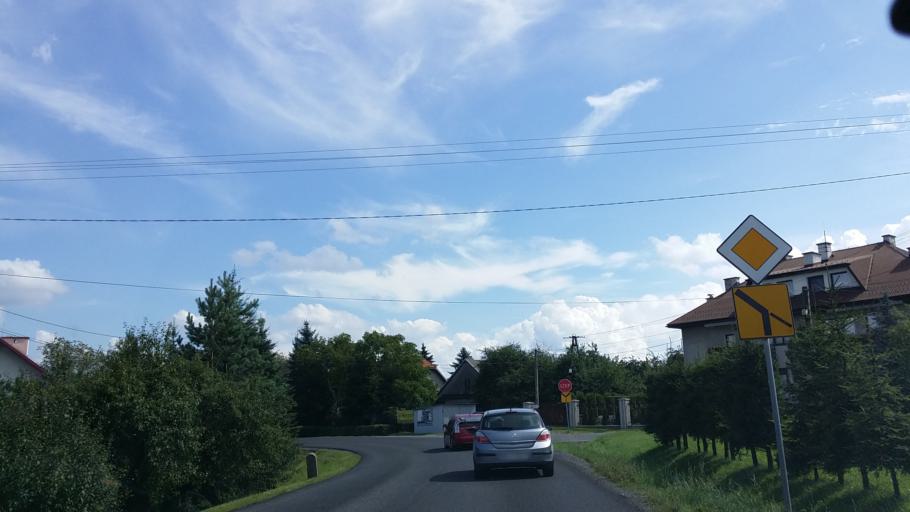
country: PL
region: Lesser Poland Voivodeship
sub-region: Powiat wielicki
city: Pawlikowice
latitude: 49.9367
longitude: 20.0561
